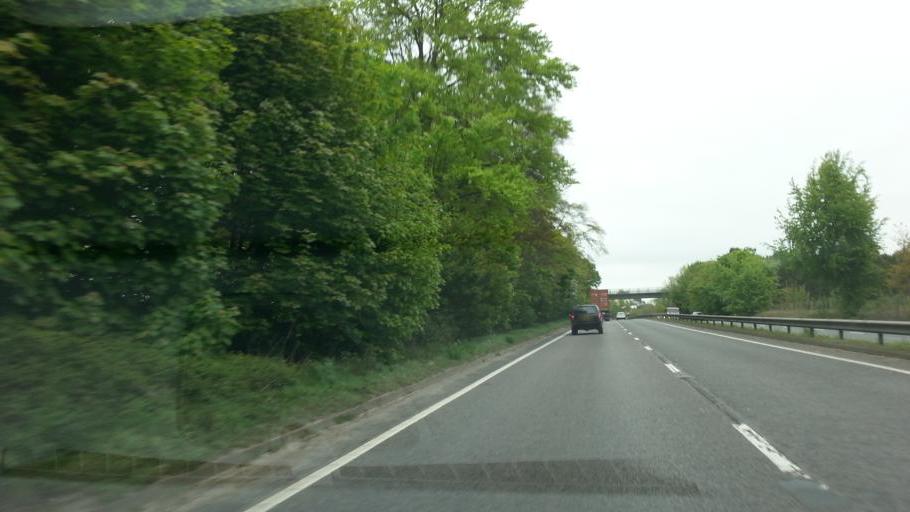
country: GB
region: England
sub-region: Suffolk
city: Thurston
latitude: 52.2370
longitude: 0.7911
